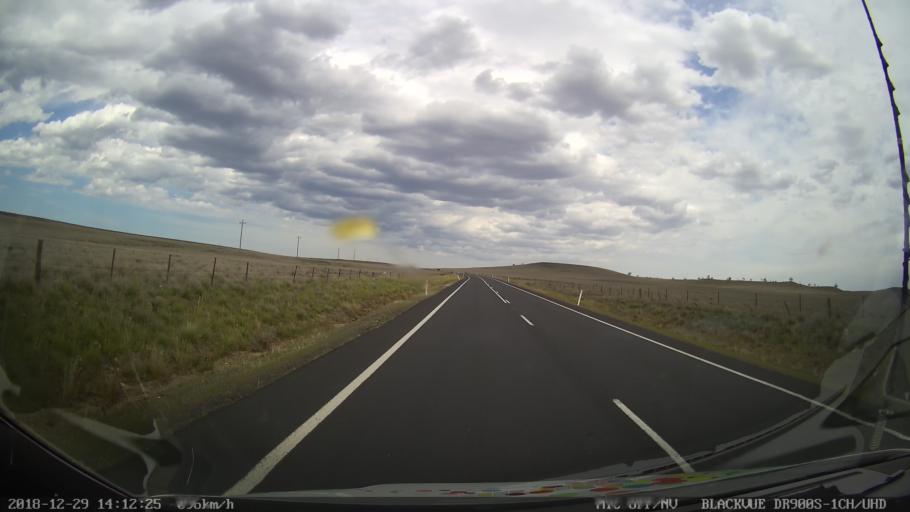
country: AU
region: New South Wales
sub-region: Cooma-Monaro
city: Cooma
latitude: -36.4154
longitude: 149.2320
